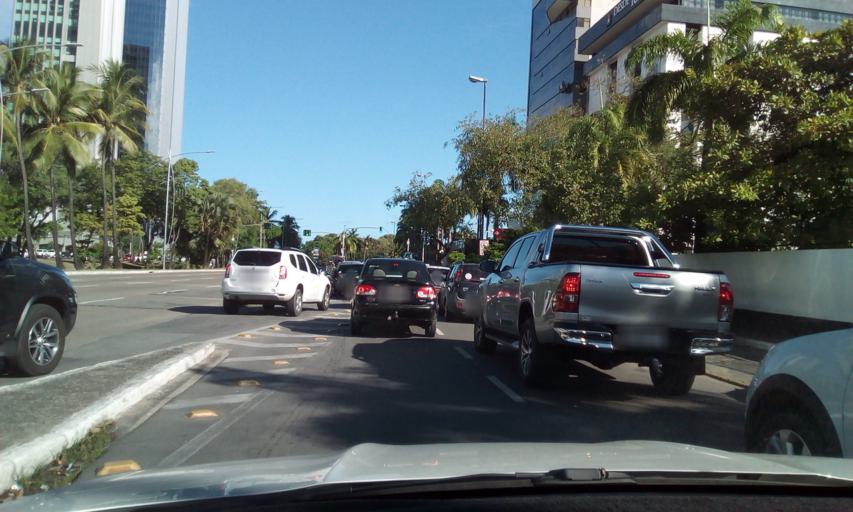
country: BR
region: Pernambuco
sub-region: Recife
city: Recife
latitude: -8.0628
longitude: -34.8978
